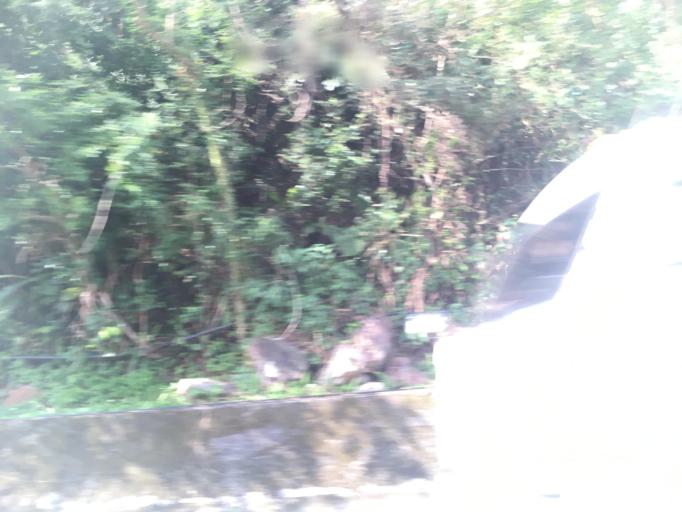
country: TW
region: Taiwan
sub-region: Yilan
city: Yilan
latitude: 24.6311
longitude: 121.5472
